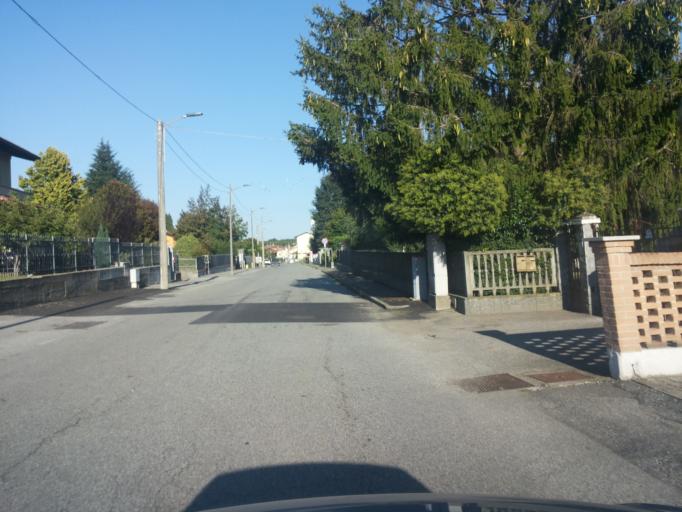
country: IT
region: Piedmont
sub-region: Provincia di Torino
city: Strambino
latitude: 45.3969
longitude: 7.8865
